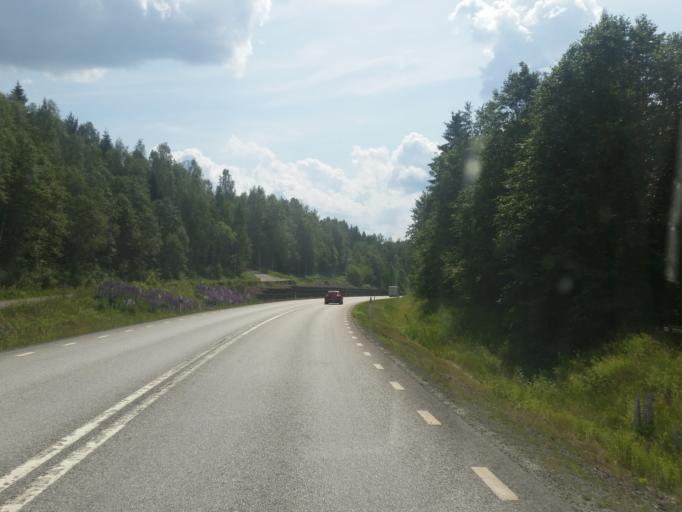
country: SE
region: OErebro
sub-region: Ljusnarsbergs Kommun
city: Kopparberg
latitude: 59.8645
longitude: 15.0582
